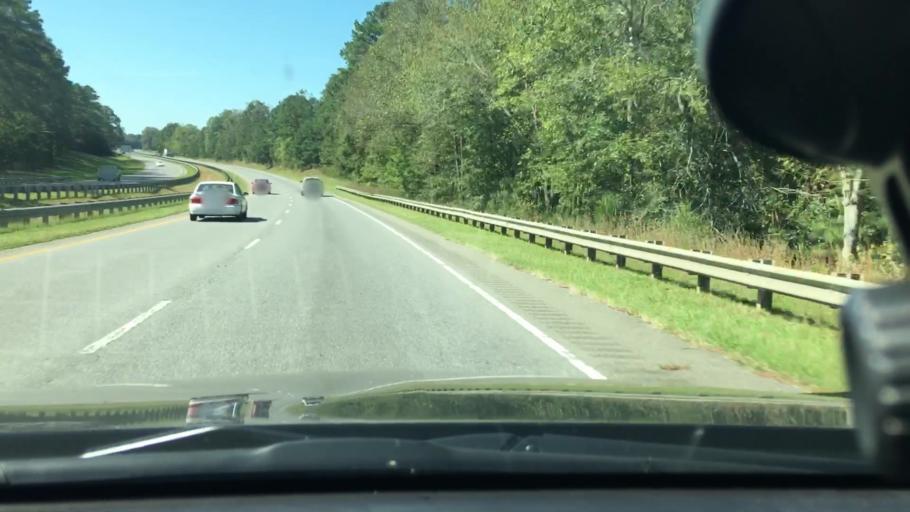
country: US
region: North Carolina
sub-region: Cleveland County
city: Boiling Springs
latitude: 35.3017
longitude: -81.7128
